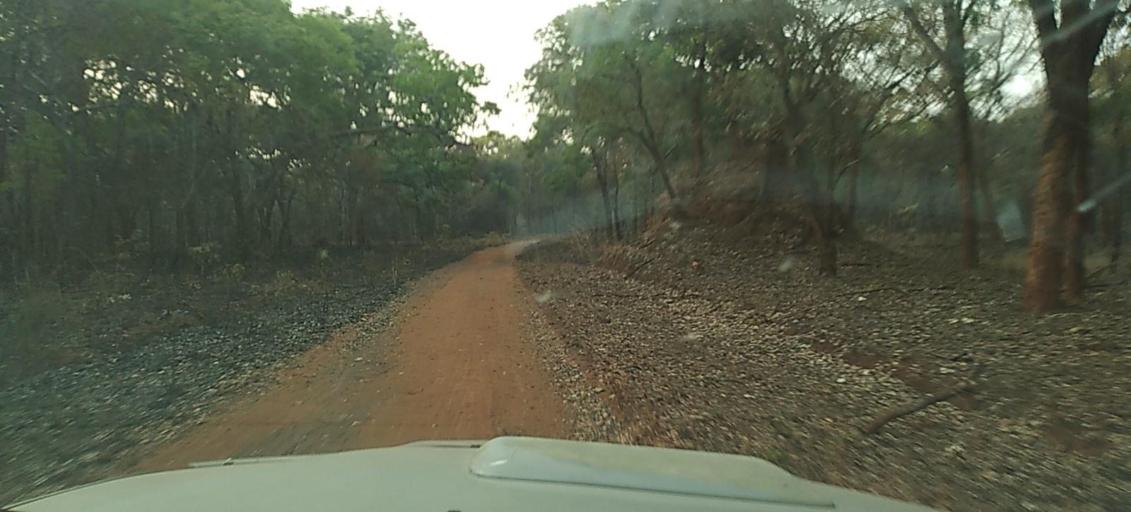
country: ZM
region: North-Western
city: Kasempa
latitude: -13.1102
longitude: 26.4054
